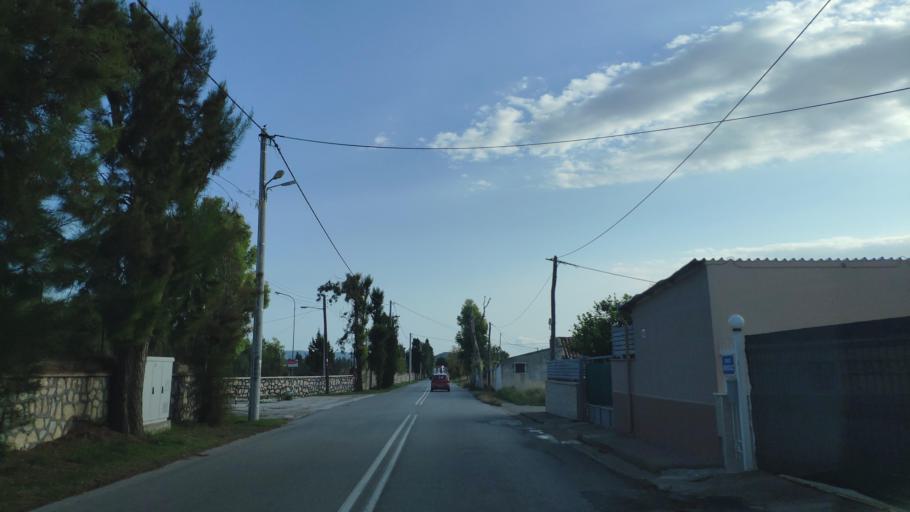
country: GR
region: Attica
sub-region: Nomarchia Dytikis Attikis
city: Megara
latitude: 37.9816
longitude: 23.3543
